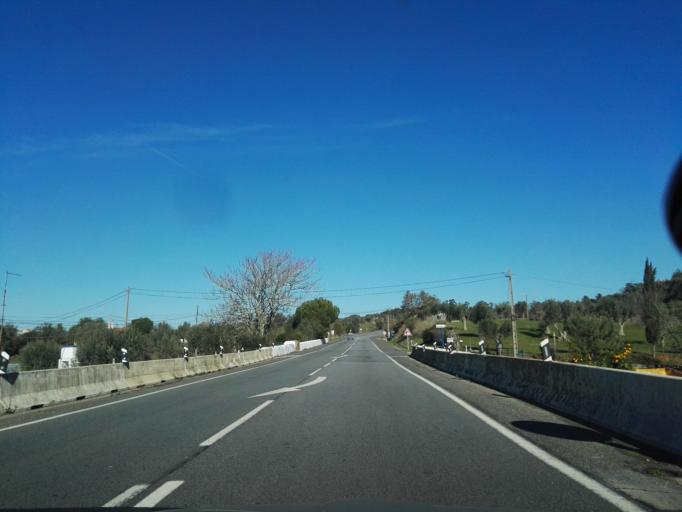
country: PT
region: Evora
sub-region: Montemor-O-Novo
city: Montemor-o-Novo
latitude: 38.6469
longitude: -8.2350
